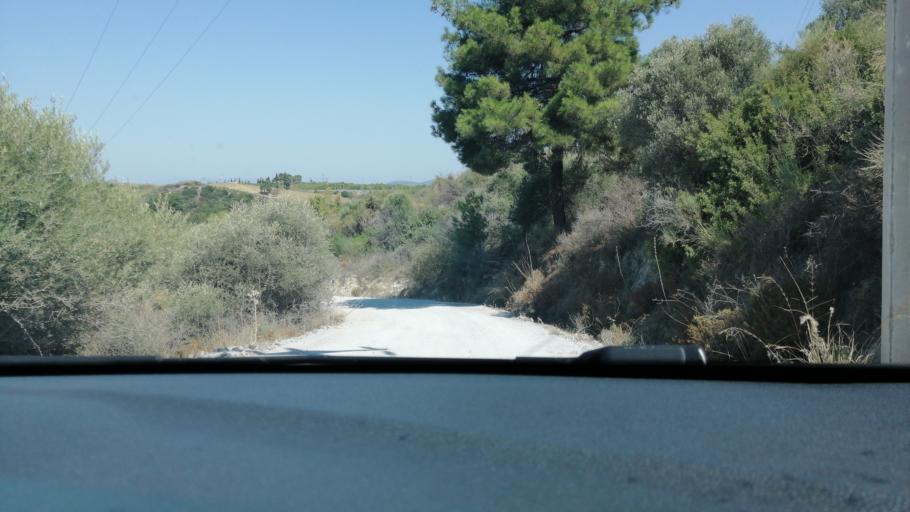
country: TR
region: Aydin
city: Davutlar
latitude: 37.7796
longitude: 27.3144
